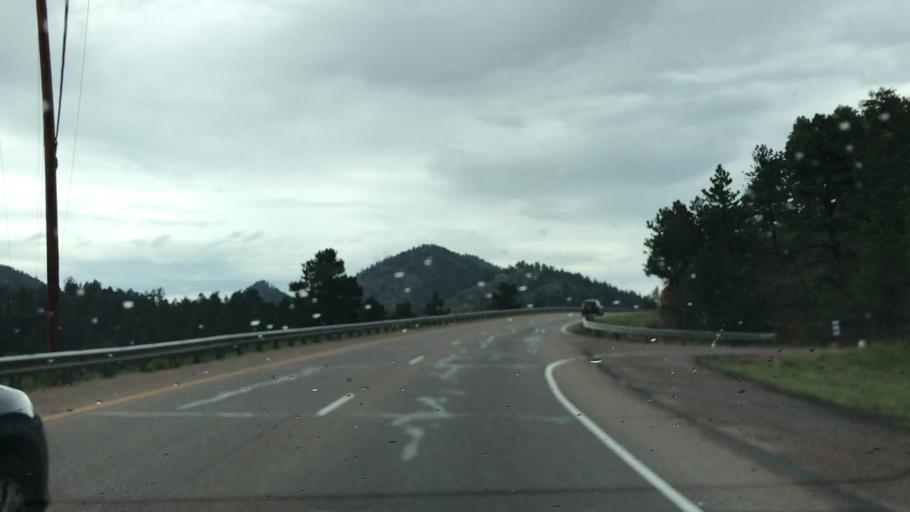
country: US
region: Colorado
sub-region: El Paso County
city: Cascade-Chipita Park
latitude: 38.9493
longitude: -105.0246
